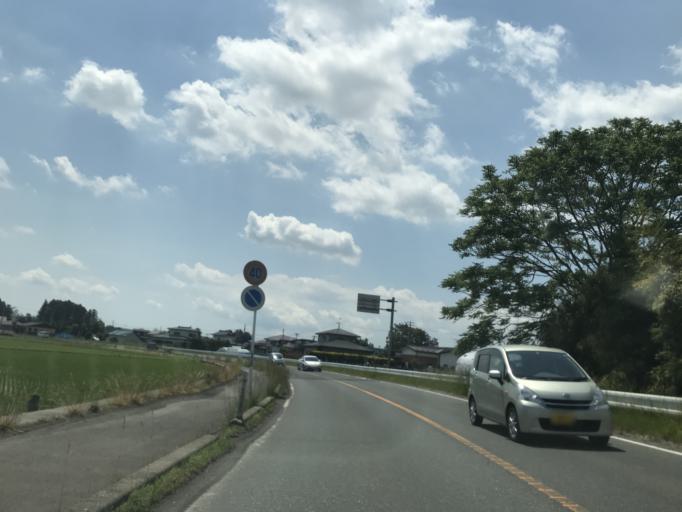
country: JP
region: Miyagi
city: Kogota
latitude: 38.5330
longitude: 141.0546
